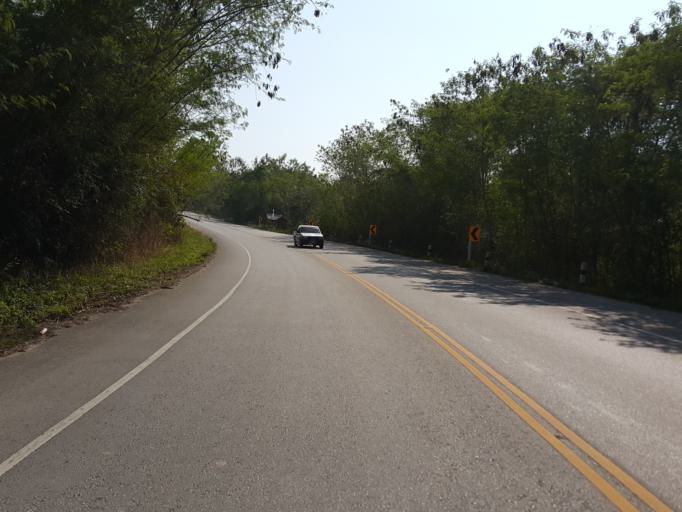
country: TH
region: Lampang
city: Mueang Pan
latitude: 18.8112
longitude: 99.5902
